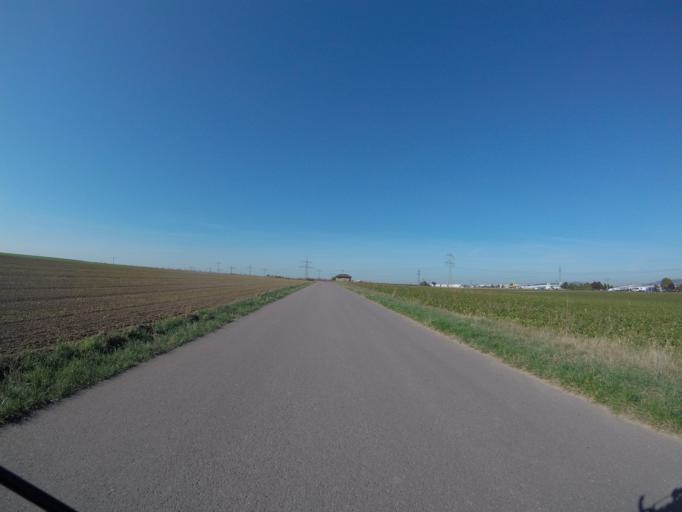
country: DE
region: Baden-Wuerttemberg
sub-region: Regierungsbezirk Stuttgart
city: Bietigheim-Bissingen
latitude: 48.9544
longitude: 9.0913
